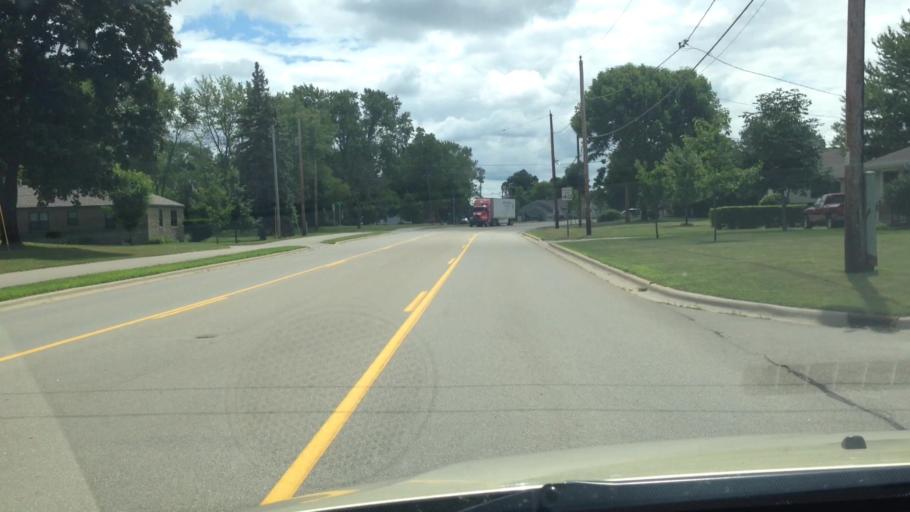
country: US
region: Michigan
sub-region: Menominee County
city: Menominee
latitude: 45.1421
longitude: -87.6034
